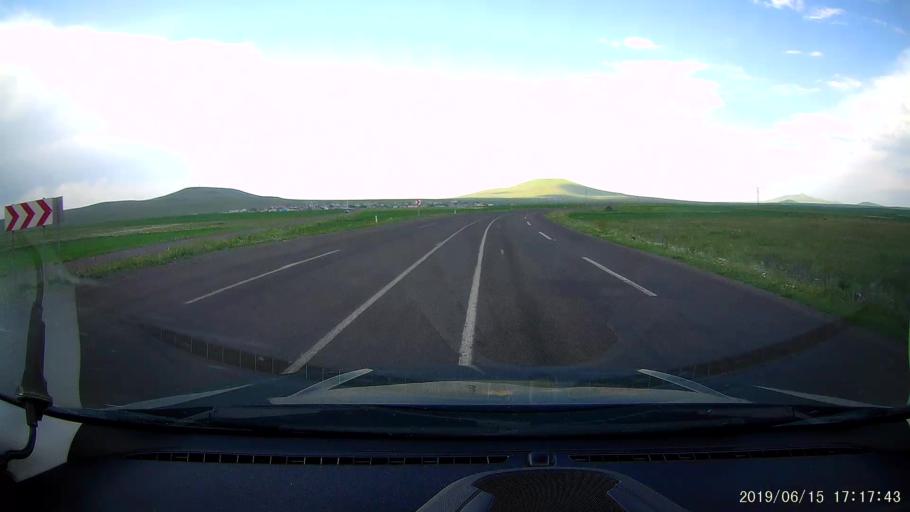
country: TR
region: Kars
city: Kars
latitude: 40.6151
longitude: 43.2442
